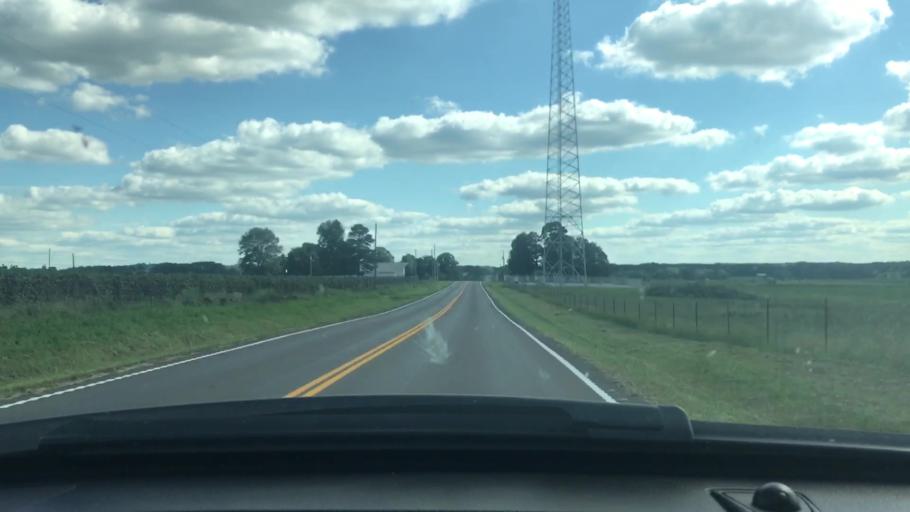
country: US
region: Missouri
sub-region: Wright County
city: Mountain Grove
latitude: 37.2491
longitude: -92.3003
